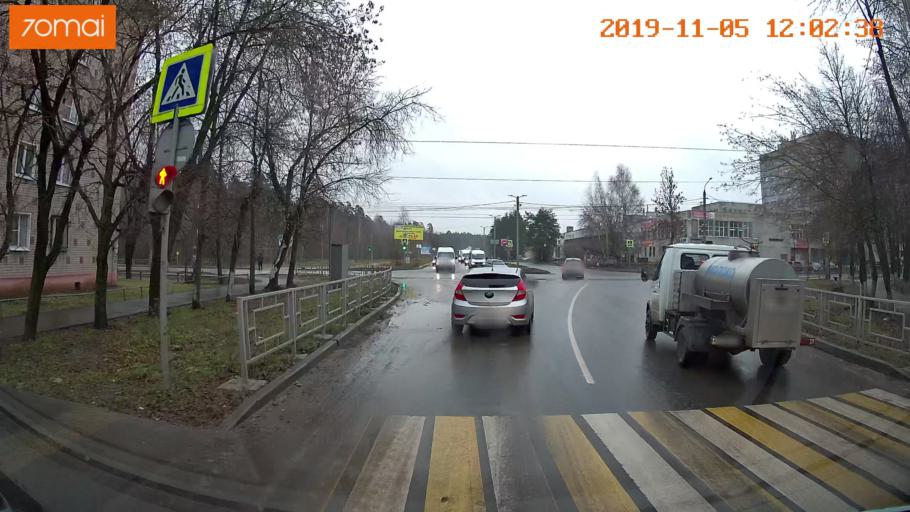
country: RU
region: Ivanovo
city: Kokhma
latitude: 56.9711
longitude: 41.0517
